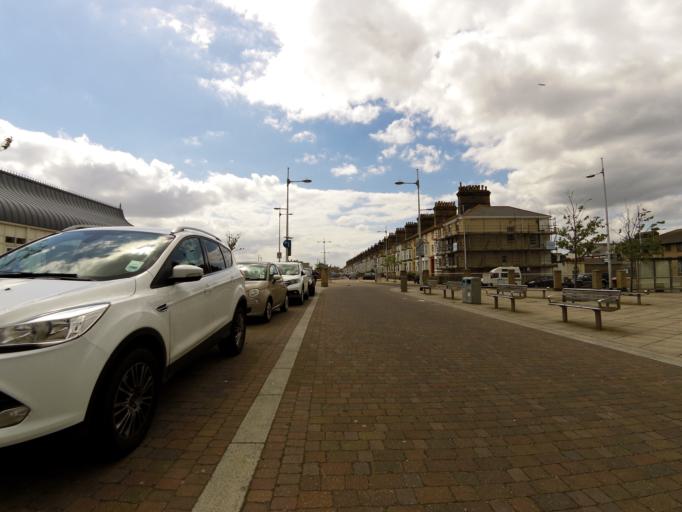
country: GB
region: England
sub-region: Suffolk
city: Lowestoft
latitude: 52.4717
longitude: 1.7495
